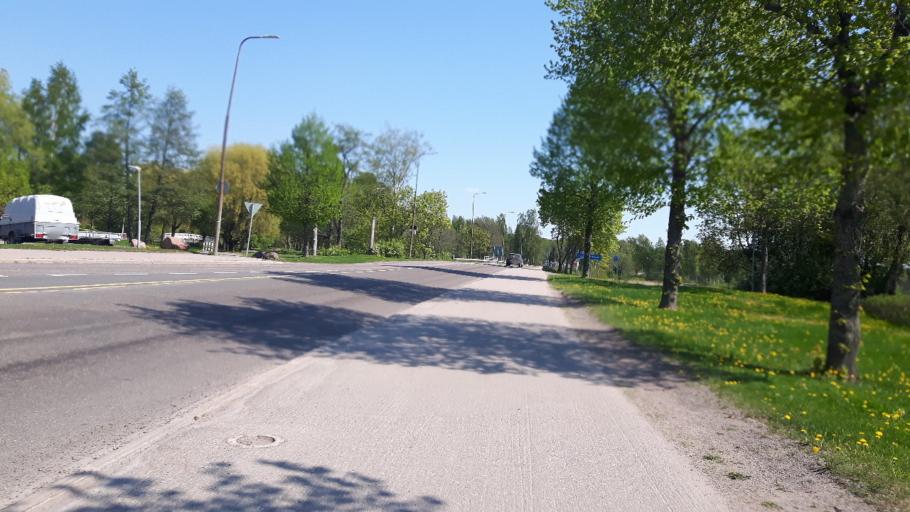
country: FI
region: Uusimaa
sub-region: Loviisa
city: Lovisa
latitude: 60.4590
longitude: 26.2324
